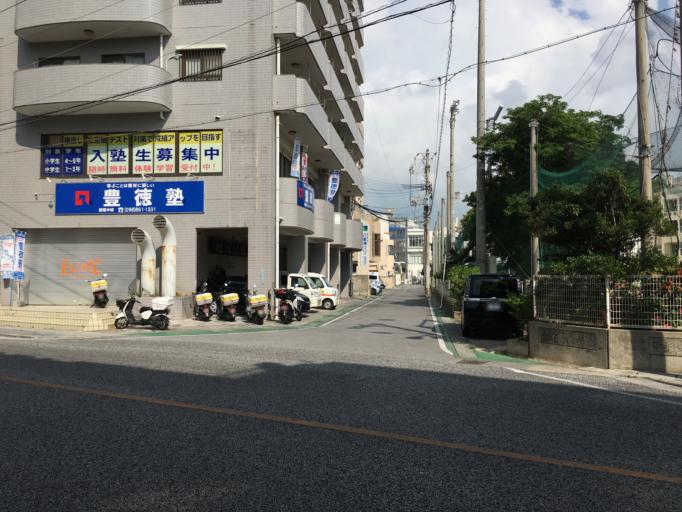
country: JP
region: Okinawa
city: Naha-shi
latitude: 26.2220
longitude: 127.6792
